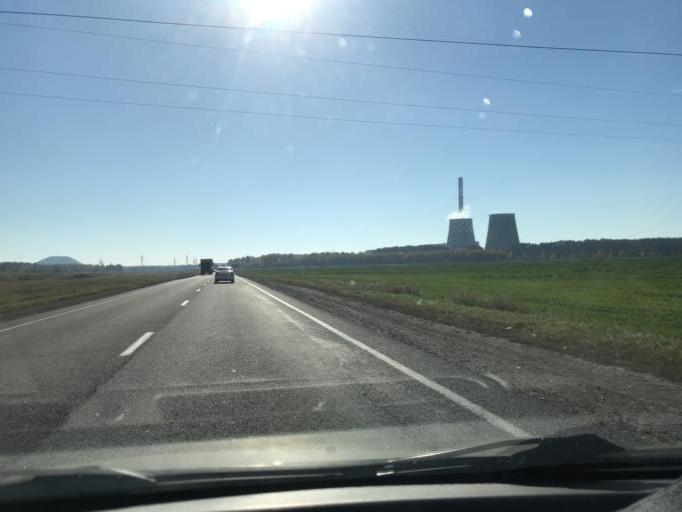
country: BY
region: Gomel
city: Kastsyukowka
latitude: 52.4606
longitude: 30.8246
